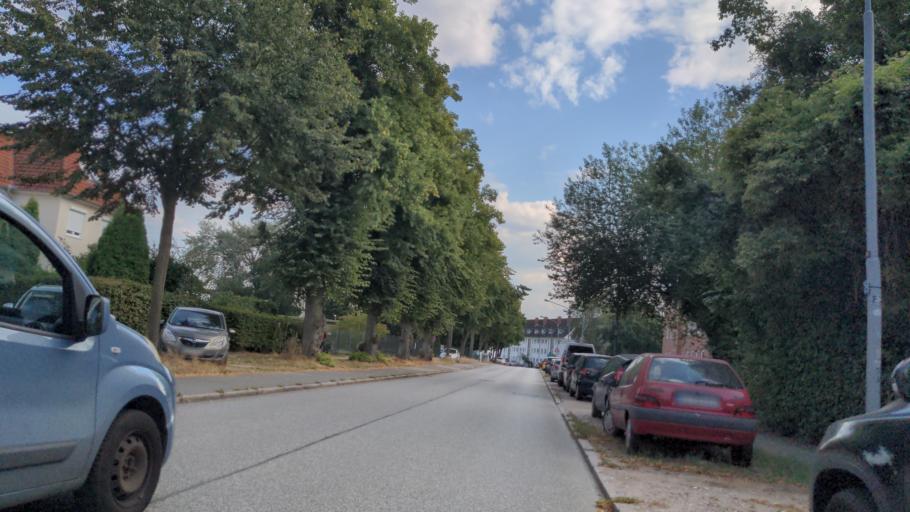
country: DE
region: Schleswig-Holstein
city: Luebeck
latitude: 53.8701
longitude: 10.7206
